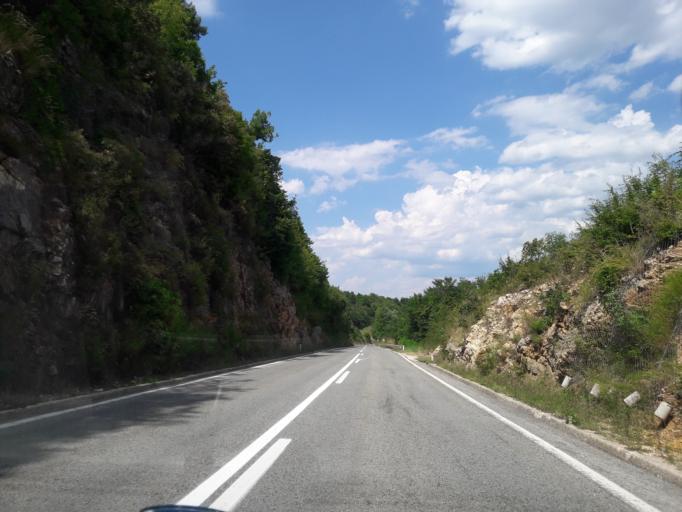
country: BA
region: Republika Srpska
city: Mrkonjic Grad
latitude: 44.5024
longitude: 17.1498
